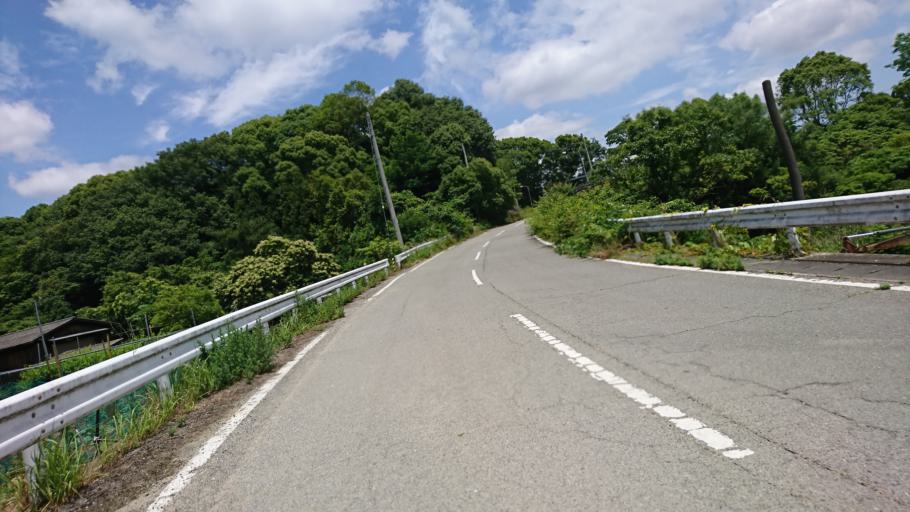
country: JP
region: Hyogo
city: Shirahamacho-usazakiminami
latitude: 34.7942
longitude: 134.7414
